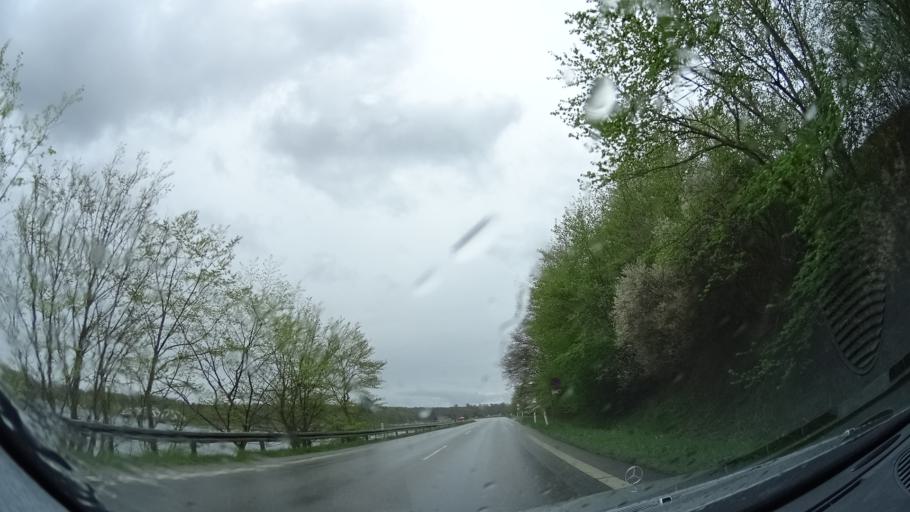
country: DK
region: Zealand
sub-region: Lejre Kommune
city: Ejby
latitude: 55.6755
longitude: 11.8065
